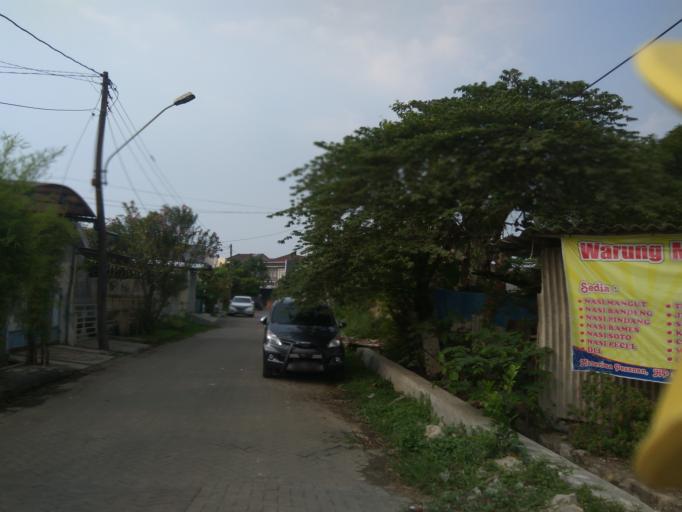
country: ID
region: Central Java
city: Semarang
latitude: -6.9697
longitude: 110.3932
